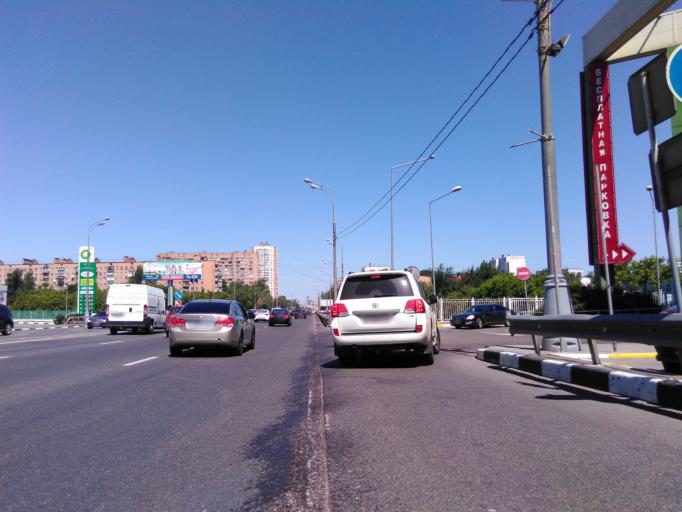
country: RU
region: Moscow
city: Novyye Cheremushki
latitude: 55.6884
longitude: 37.6043
